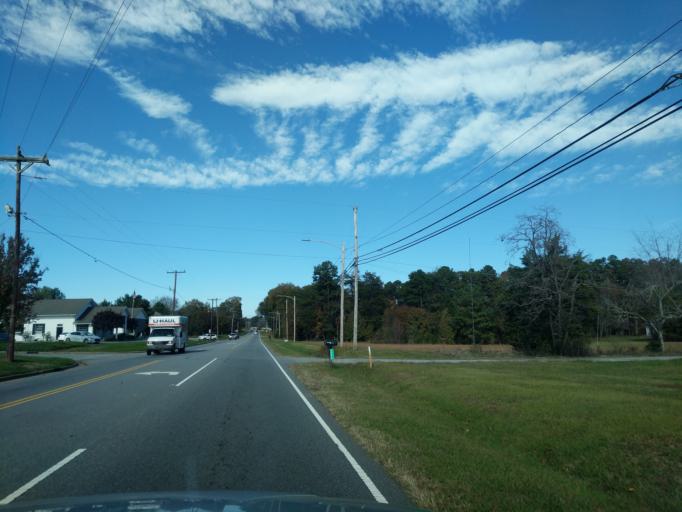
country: US
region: North Carolina
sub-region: Catawba County
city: Newton
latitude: 35.6381
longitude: -81.2680
